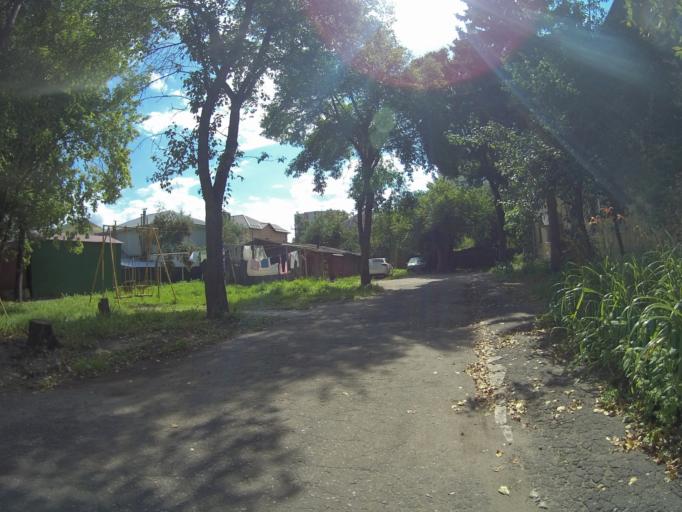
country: RU
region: Vladimir
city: Vladimir
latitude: 56.1203
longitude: 40.3820
